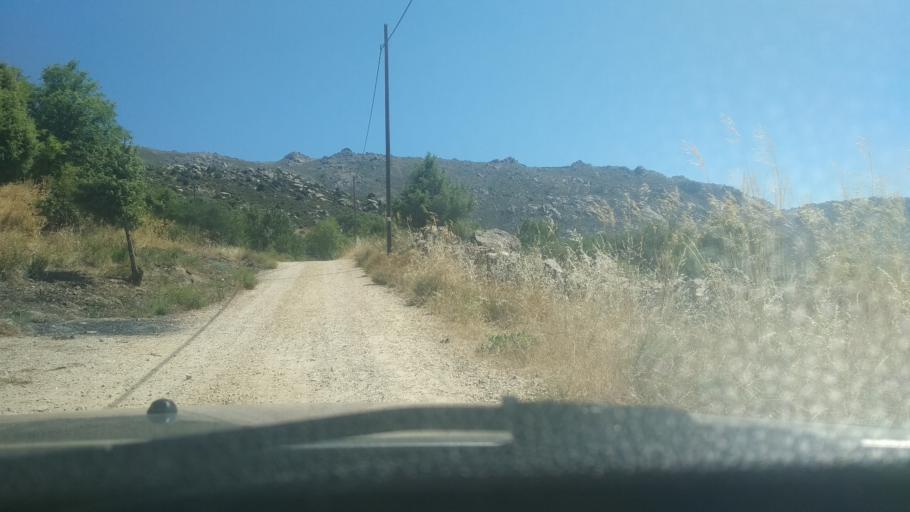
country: ES
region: Madrid
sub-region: Provincia de Madrid
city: Becerril de la Sierra
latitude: 40.7356
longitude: -3.9568
